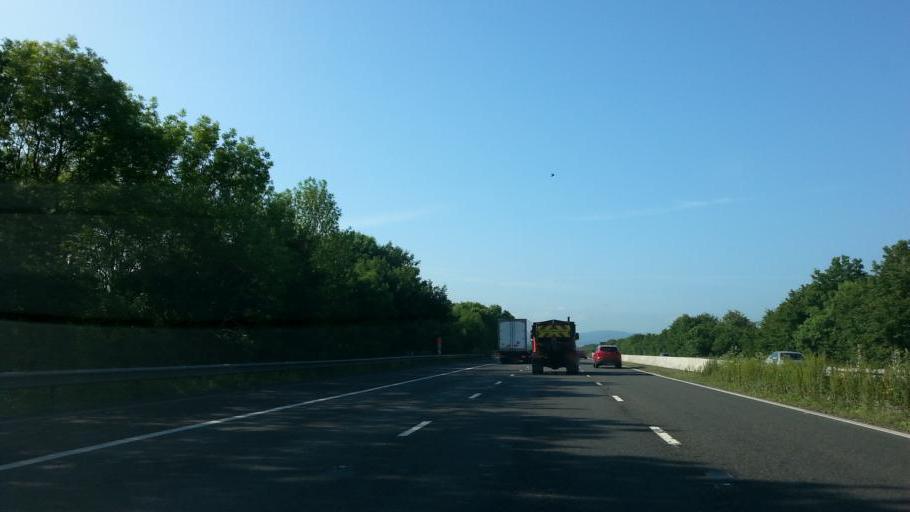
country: GB
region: England
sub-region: Gloucestershire
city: Churchdown
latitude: 51.9021
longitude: -2.1516
